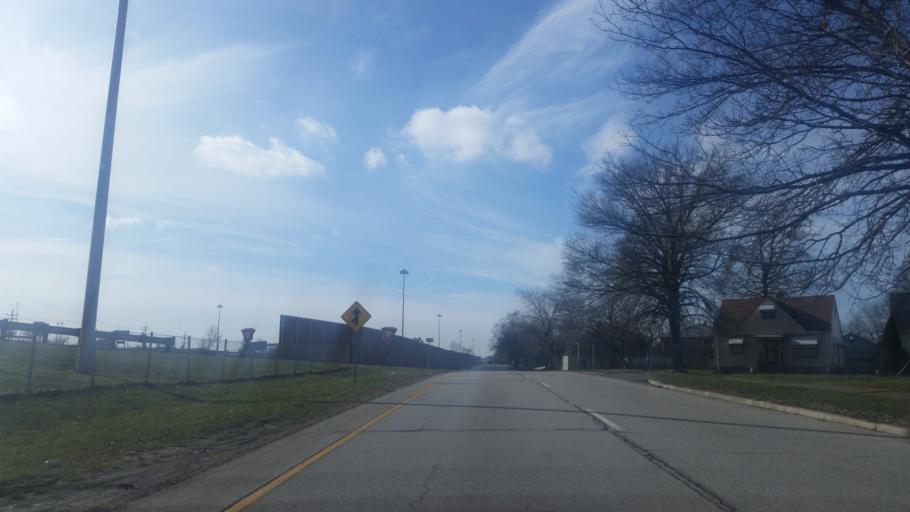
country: US
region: Ohio
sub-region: Cuyahoga County
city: Euclid
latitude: 41.5872
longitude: -81.5283
